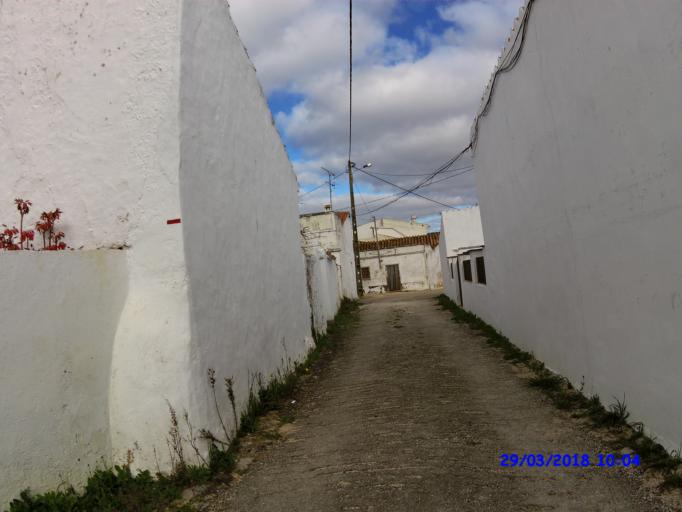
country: PT
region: Faro
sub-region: Loule
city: Boliqueime
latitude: 37.2316
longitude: -8.1619
